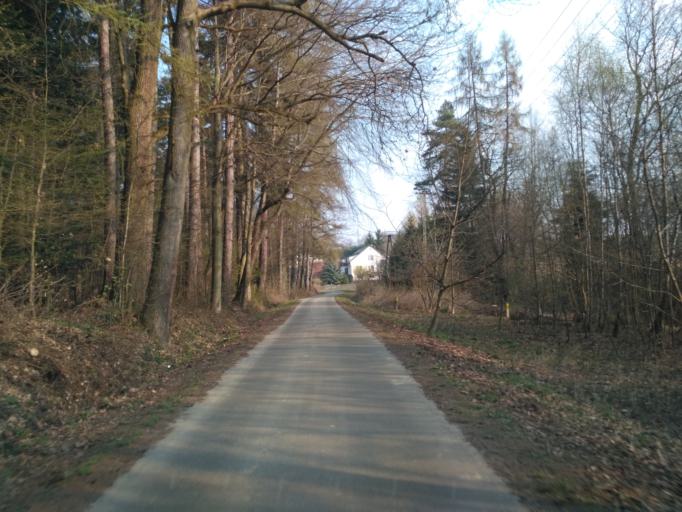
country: PL
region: Subcarpathian Voivodeship
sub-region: Powiat strzyzowski
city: Wisniowa
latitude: 49.8827
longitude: 21.6348
